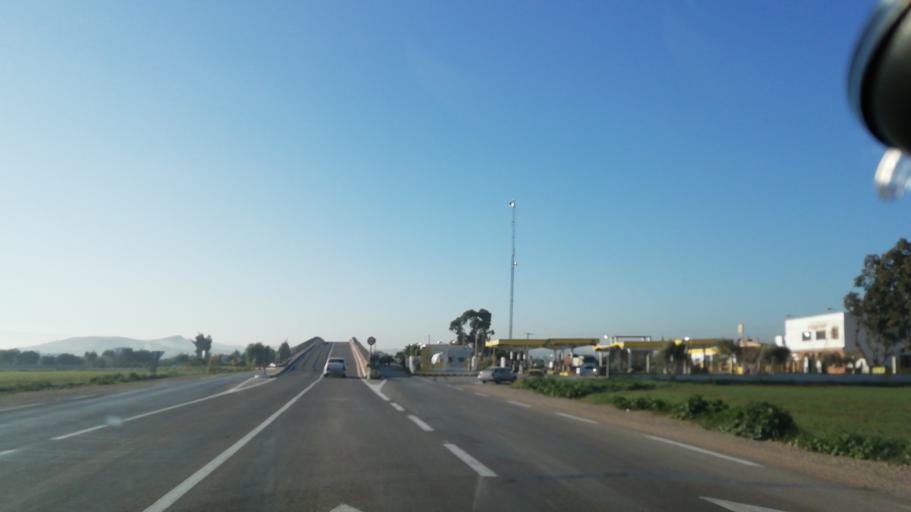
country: DZ
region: Tlemcen
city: Remchi
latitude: 35.0491
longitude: -1.5031
